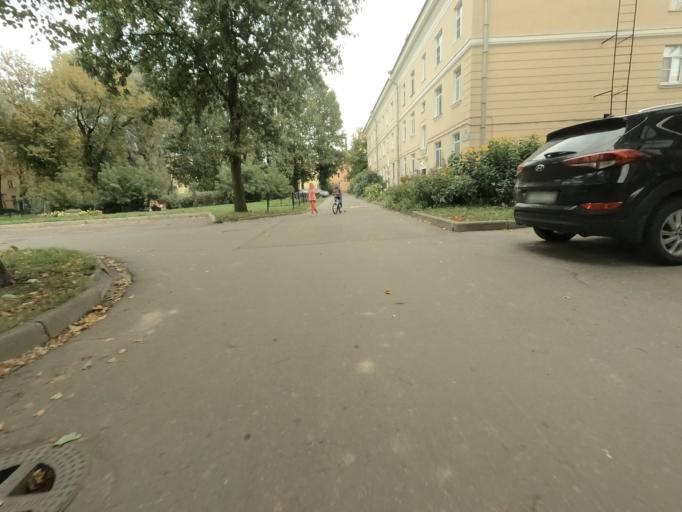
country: RU
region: St.-Petersburg
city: Pontonnyy
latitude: 59.7850
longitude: 30.6232
